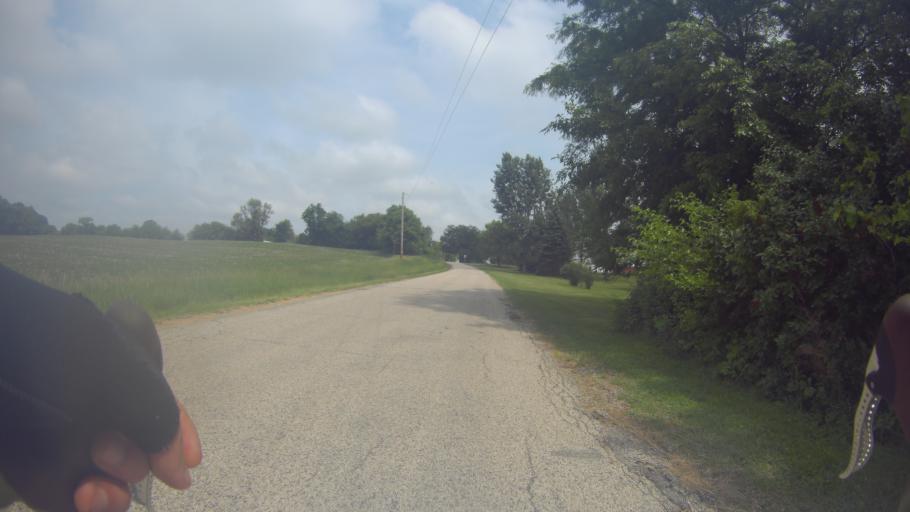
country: US
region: Wisconsin
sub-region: Jefferson County
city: Lake Ripley
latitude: 42.9340
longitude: -88.9888
